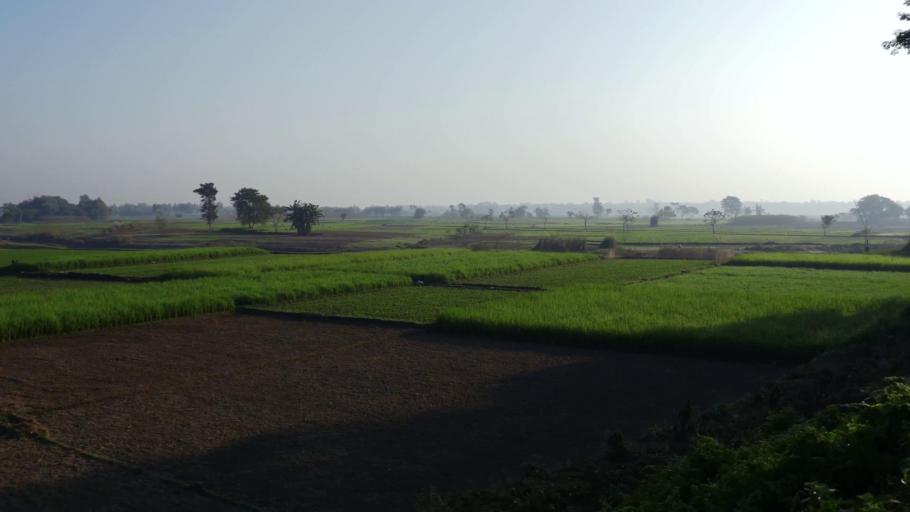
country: BD
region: Dhaka
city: Jamalpur
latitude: 24.9228
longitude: 89.9394
